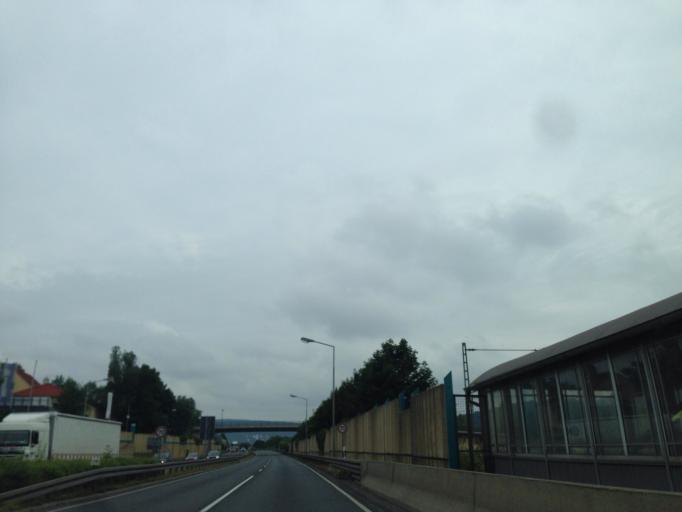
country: DE
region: Thuringia
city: Rudolstadt
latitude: 50.6916
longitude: 11.3278
